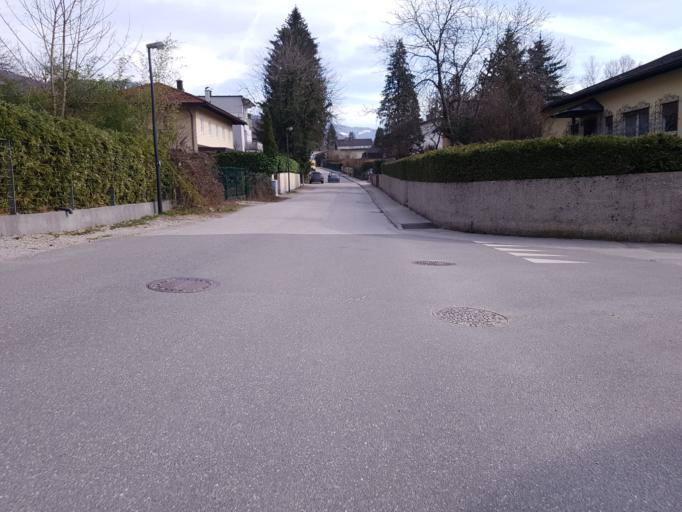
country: AT
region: Salzburg
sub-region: Salzburg Stadt
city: Salzburg
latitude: 47.8062
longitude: 13.0760
